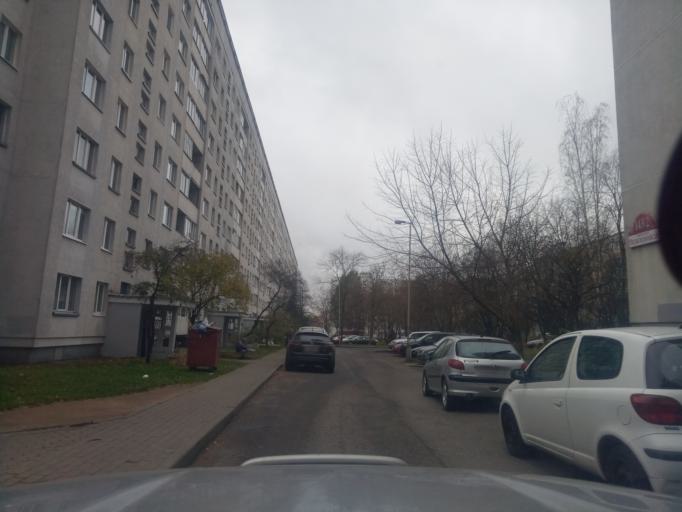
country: BY
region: Minsk
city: Borovlyany
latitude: 53.9342
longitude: 27.6463
